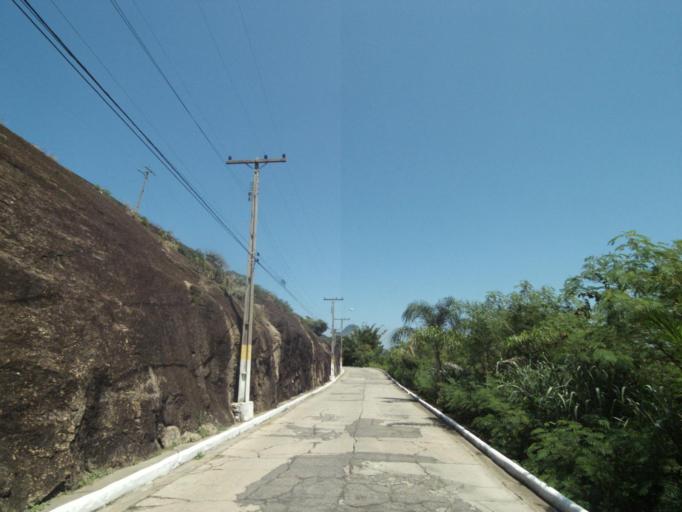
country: BR
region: Rio de Janeiro
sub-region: Niteroi
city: Niteroi
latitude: -22.9357
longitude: -43.1269
